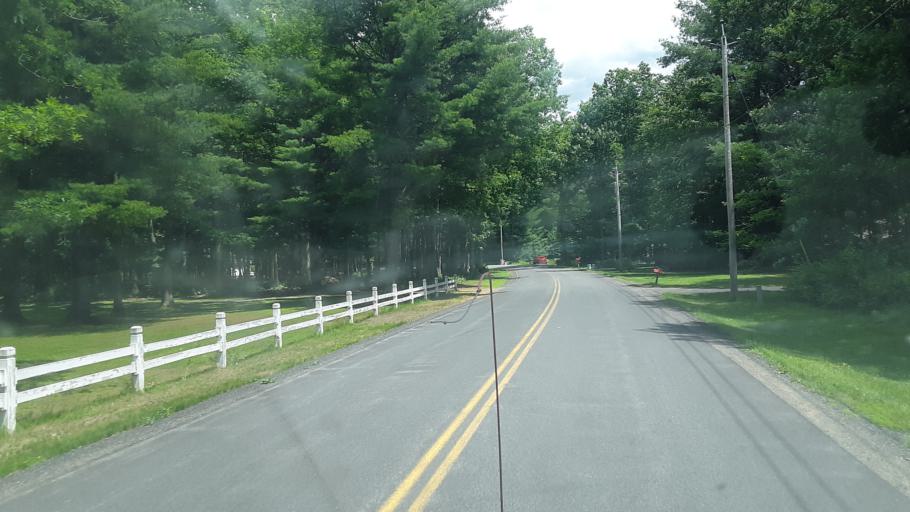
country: US
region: New York
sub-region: Oneida County
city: Rome
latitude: 43.2634
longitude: -75.5652
